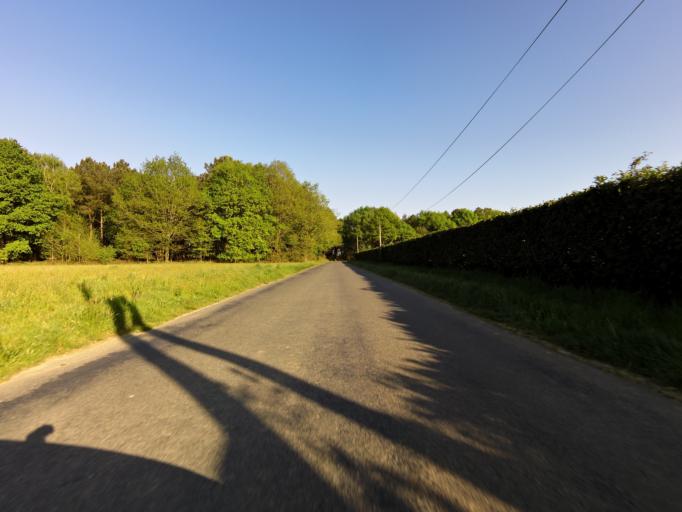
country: FR
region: Brittany
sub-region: Departement du Morbihan
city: Molac
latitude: 47.7390
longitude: -2.4508
